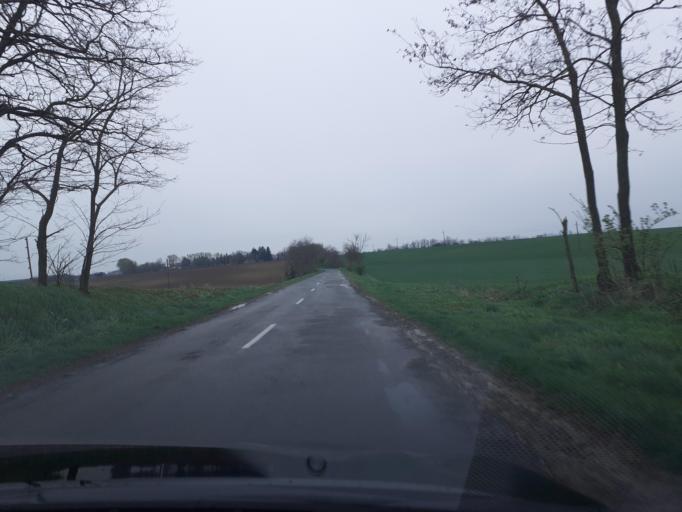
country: HU
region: Tolna
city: Hogyesz
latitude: 46.4406
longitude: 18.4576
